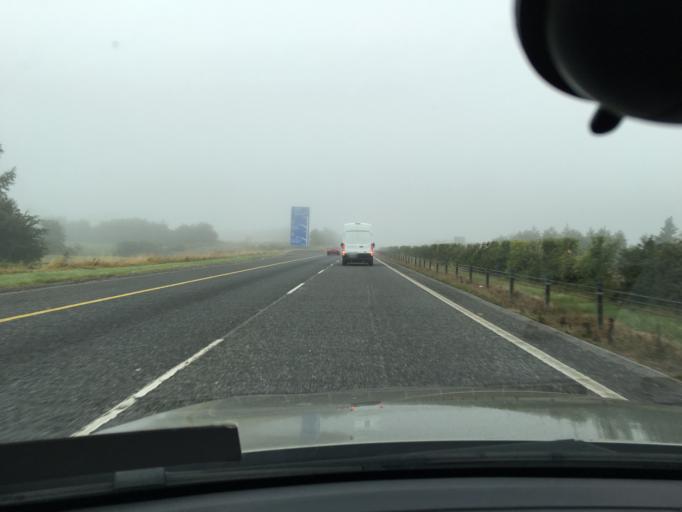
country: IE
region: Leinster
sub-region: An Iarmhi
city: Kinnegad
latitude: 53.4462
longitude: -7.0740
